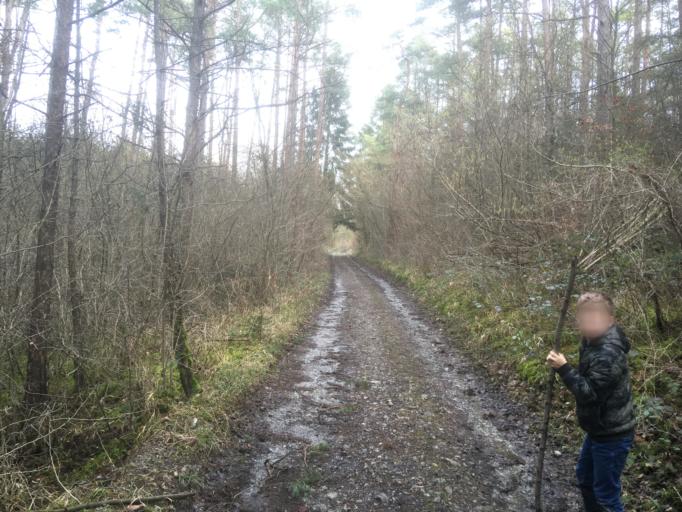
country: BE
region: Wallonia
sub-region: Province du Luxembourg
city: Durbuy
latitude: 50.3176
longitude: 5.4967
